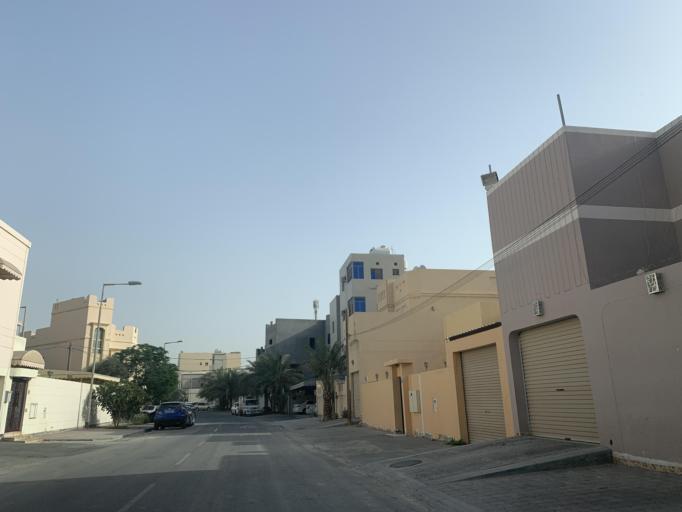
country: BH
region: Northern
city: Madinat `Isa
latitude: 26.1585
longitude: 50.5076
